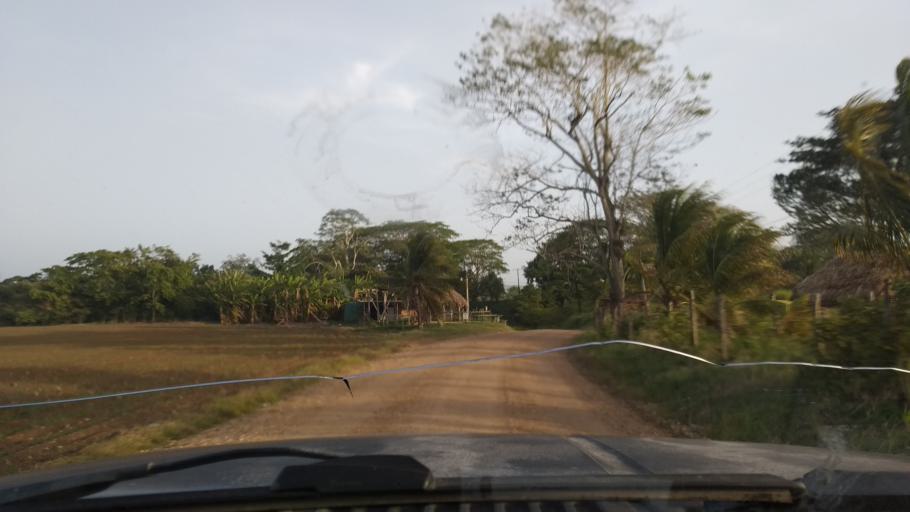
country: BZ
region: Cayo
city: San Ignacio
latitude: 17.2068
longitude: -89.0138
